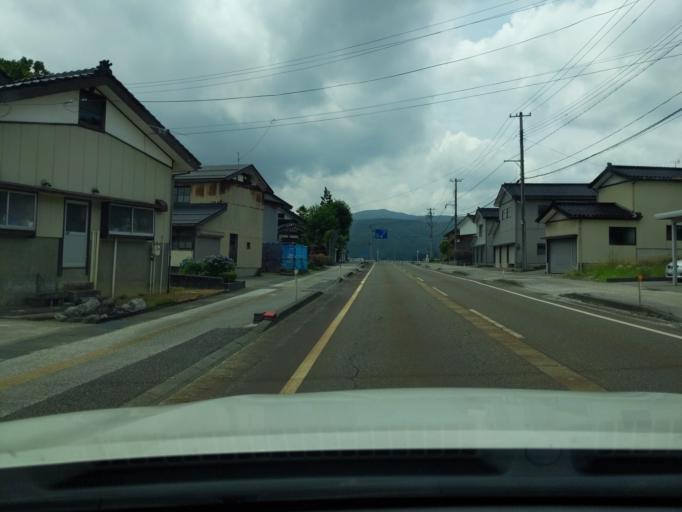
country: JP
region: Niigata
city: Kashiwazaki
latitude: 37.3311
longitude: 138.5760
